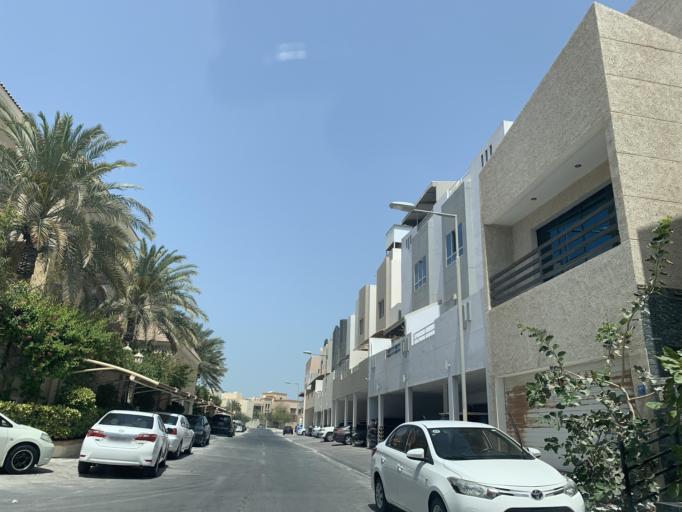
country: BH
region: Muharraq
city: Al Muharraq
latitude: 26.2782
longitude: 50.6098
